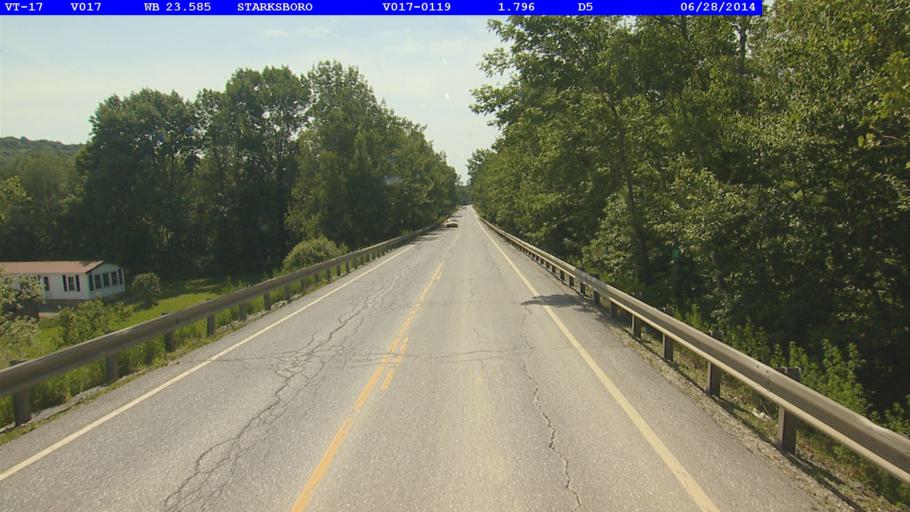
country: US
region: Vermont
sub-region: Addison County
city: Bristol
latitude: 44.1704
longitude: -72.9854
